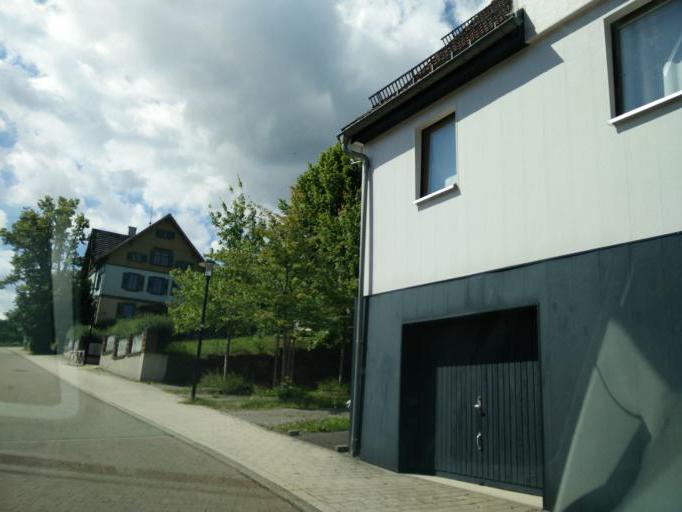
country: DE
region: Baden-Wuerttemberg
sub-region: Karlsruhe Region
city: Engelsbrand
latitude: 48.8306
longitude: 8.6434
